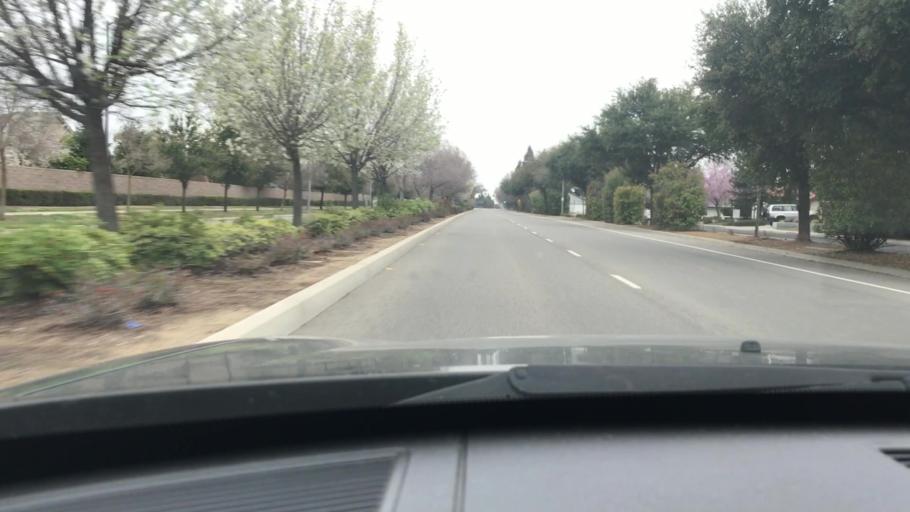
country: US
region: California
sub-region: Fresno County
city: Clovis
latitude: 36.8262
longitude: -119.6640
